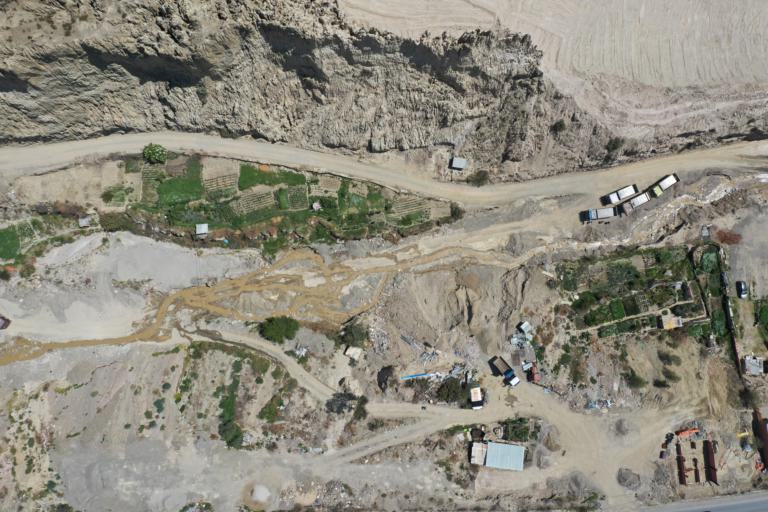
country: BO
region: La Paz
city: La Paz
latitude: -16.5633
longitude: -68.1113
